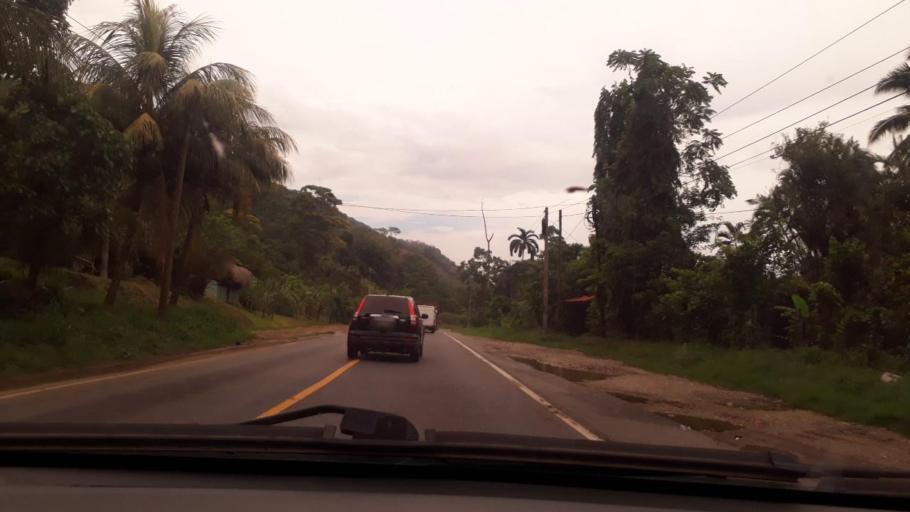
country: GT
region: Izabal
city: Morales
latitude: 15.5404
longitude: -88.7323
